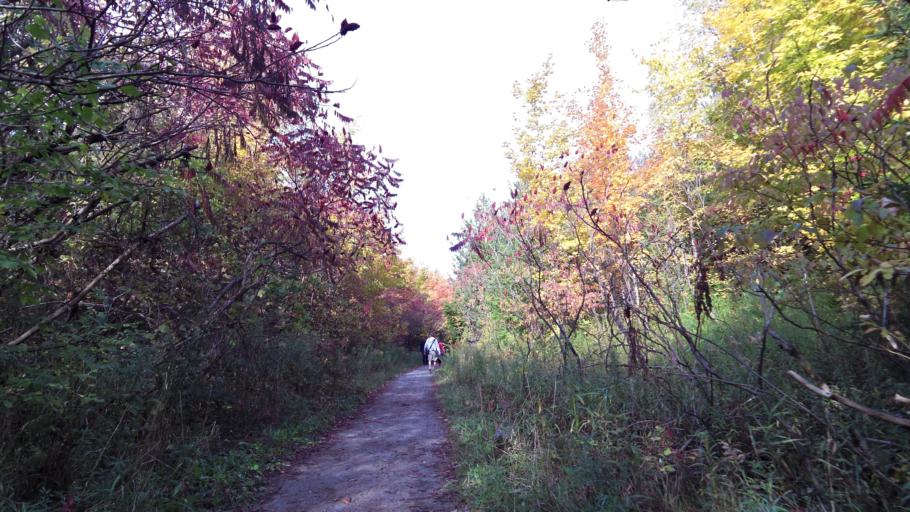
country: CA
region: Ontario
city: Orangeville
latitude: 43.8191
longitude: -80.0256
